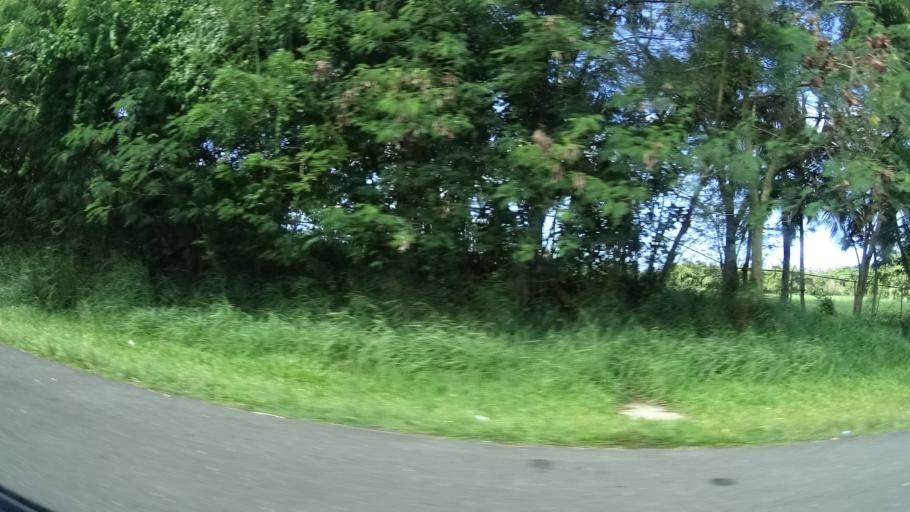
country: PR
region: Luquillo
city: Playa Fortuna
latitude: 18.3767
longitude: -65.7552
